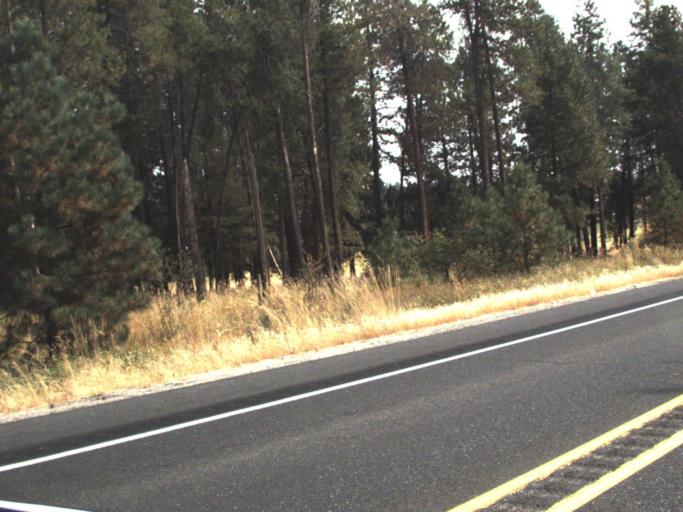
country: US
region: Washington
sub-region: Spokane County
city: Deer Park
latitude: 47.9563
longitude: -117.4905
